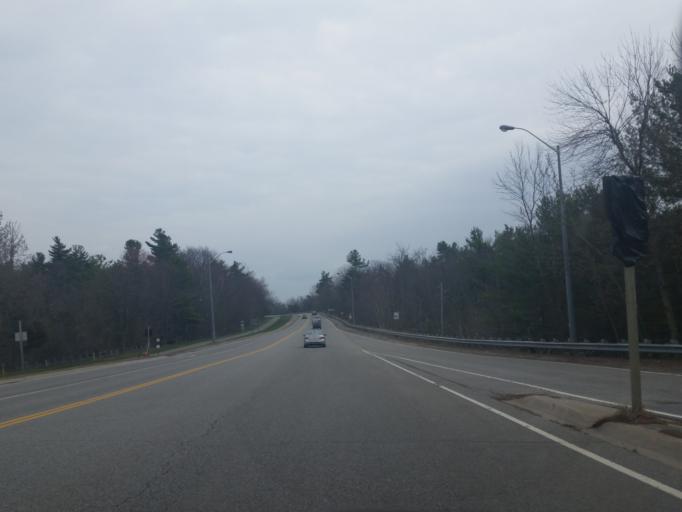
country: US
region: New York
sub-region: Jefferson County
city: Alexandria Bay
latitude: 44.3686
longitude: -75.9760
